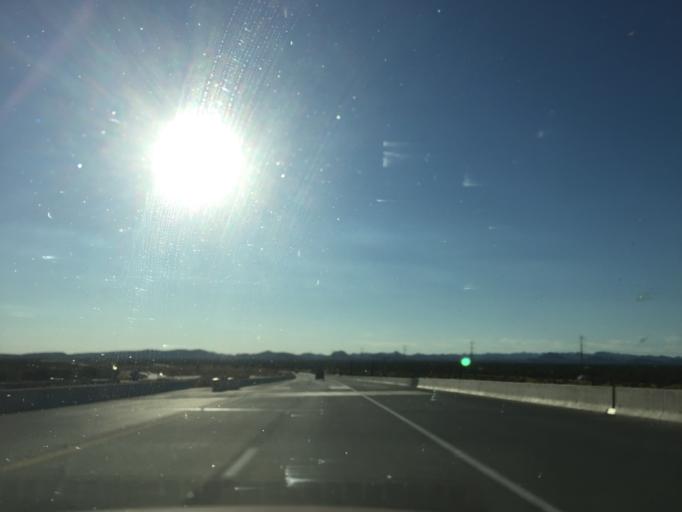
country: US
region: Arizona
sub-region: Maricopa County
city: Anthem
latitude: 33.7817
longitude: -112.1934
